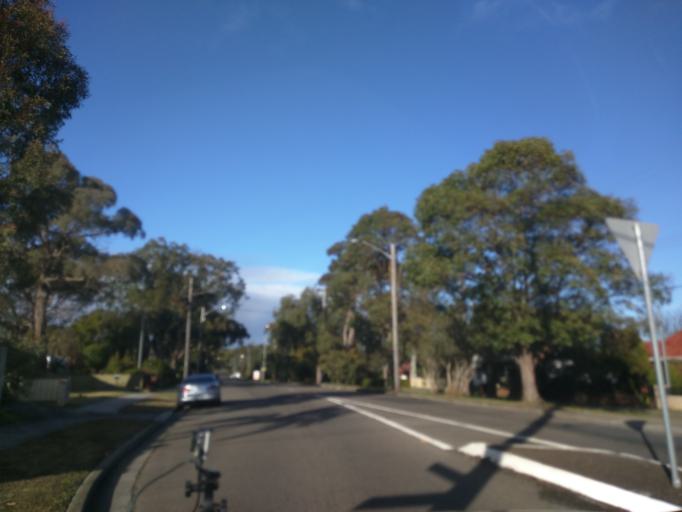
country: AU
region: New South Wales
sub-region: Hurstville
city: Peakhurst
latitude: -33.9671
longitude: 151.0496
